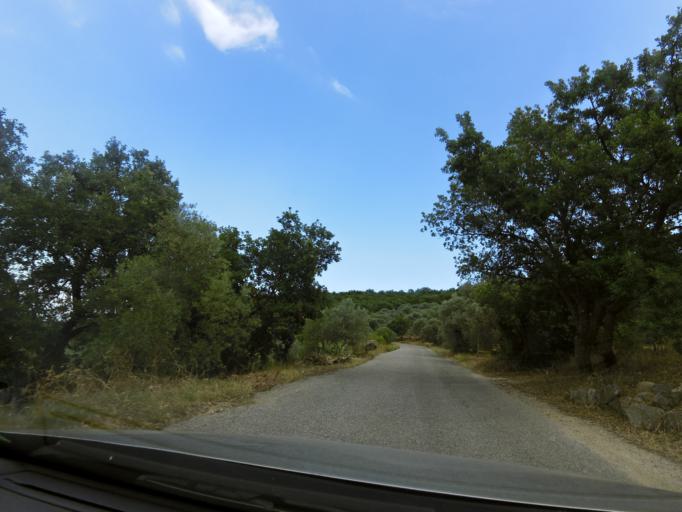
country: IT
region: Calabria
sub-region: Provincia di Reggio Calabria
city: Camini
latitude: 38.4328
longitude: 16.5013
